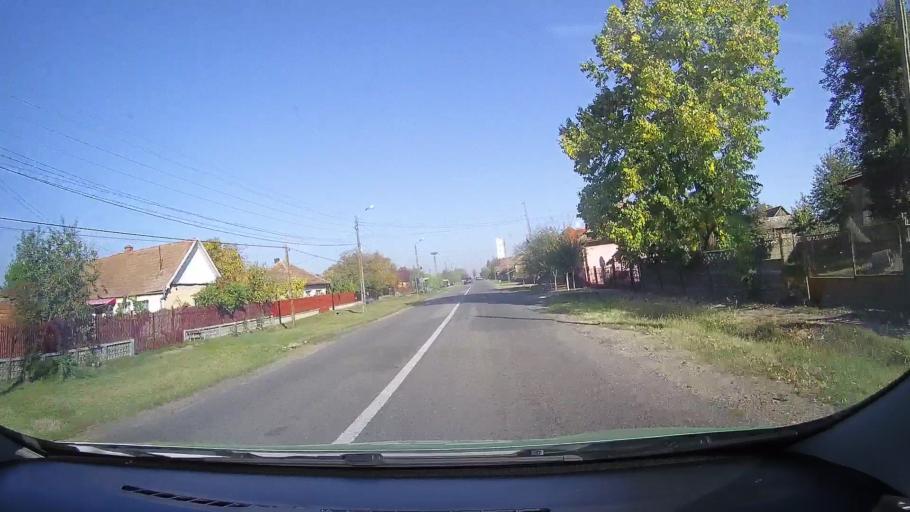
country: RO
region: Satu Mare
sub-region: Oras Tasnad
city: Tasnad
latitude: 47.5103
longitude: 22.5730
